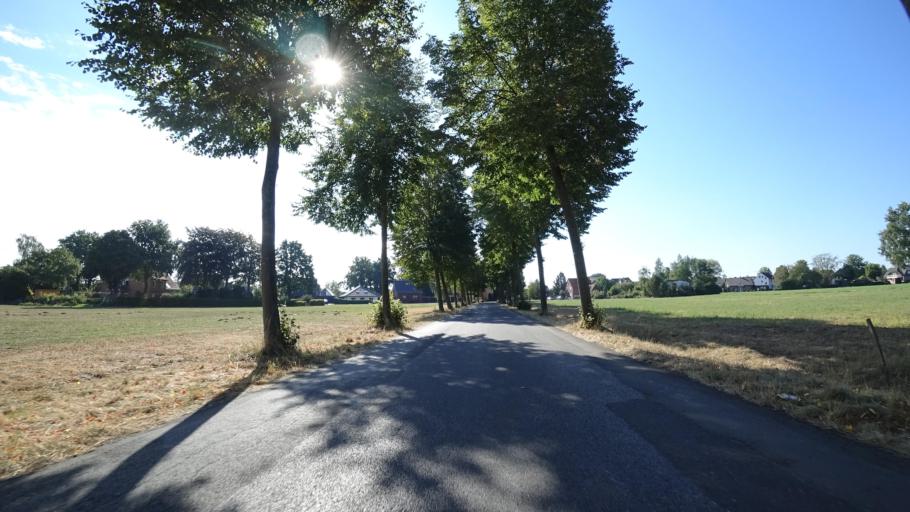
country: DE
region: North Rhine-Westphalia
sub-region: Regierungsbezirk Detmold
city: Rheda-Wiedenbruck
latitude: 51.8643
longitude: 8.2787
